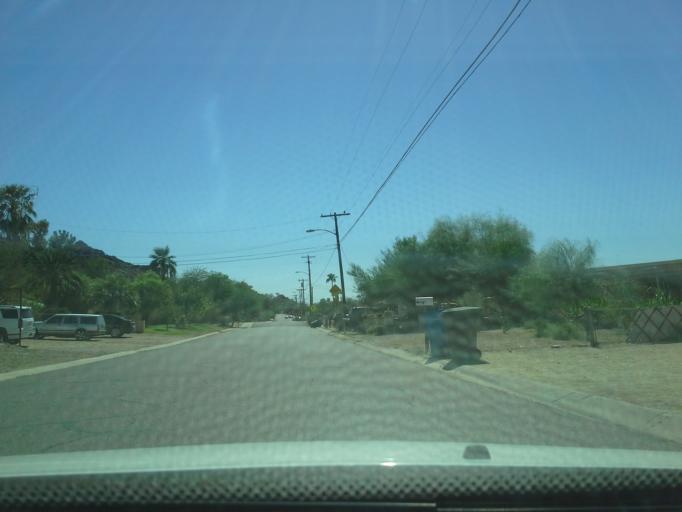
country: US
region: Arizona
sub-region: Maricopa County
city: Paradise Valley
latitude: 33.5712
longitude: -112.0525
